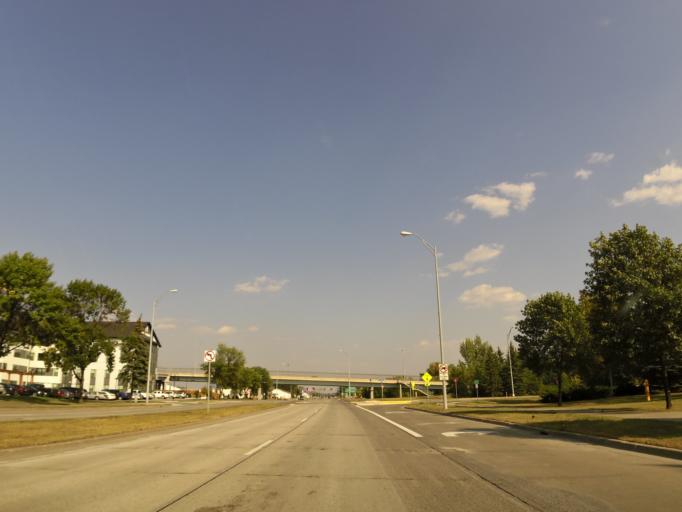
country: US
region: North Dakota
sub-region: Grand Forks County
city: Grand Forks
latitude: 47.9163
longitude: -97.0690
